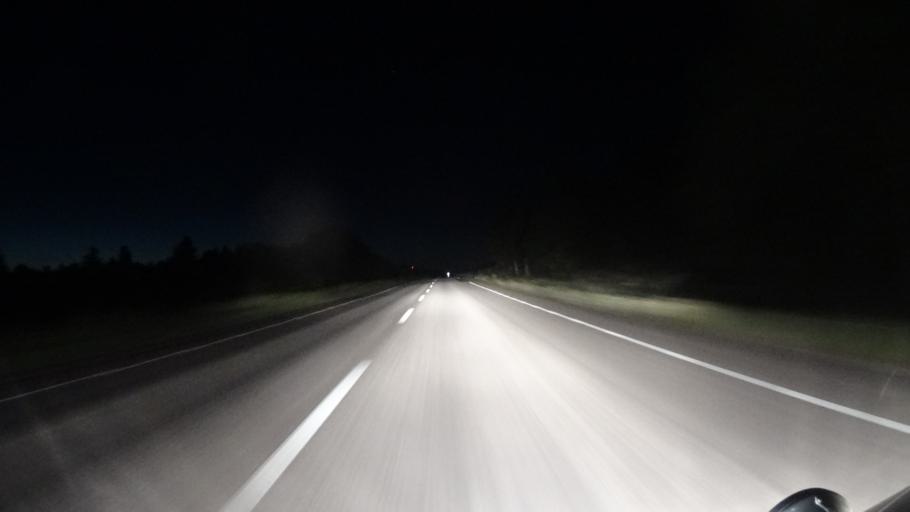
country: SE
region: OEstergoetland
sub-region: Odeshogs Kommun
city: OEdeshoeg
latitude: 58.2548
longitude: 14.7329
